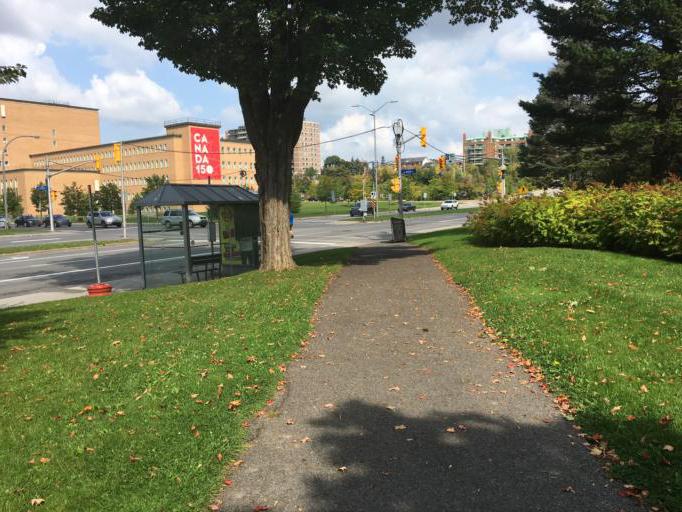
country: CA
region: Ontario
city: Ottawa
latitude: 45.3987
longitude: -75.7045
